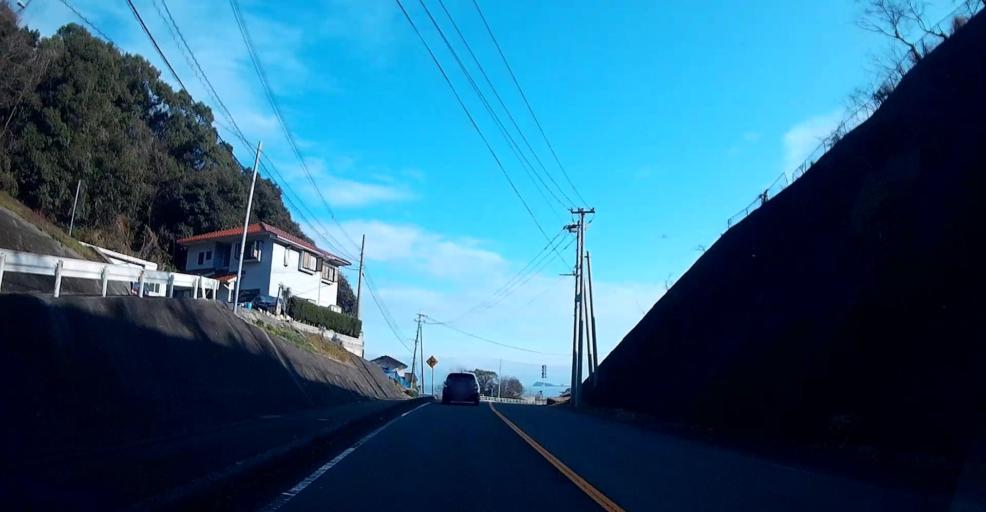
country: JP
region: Kumamoto
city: Yatsushiro
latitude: 32.5172
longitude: 130.4550
